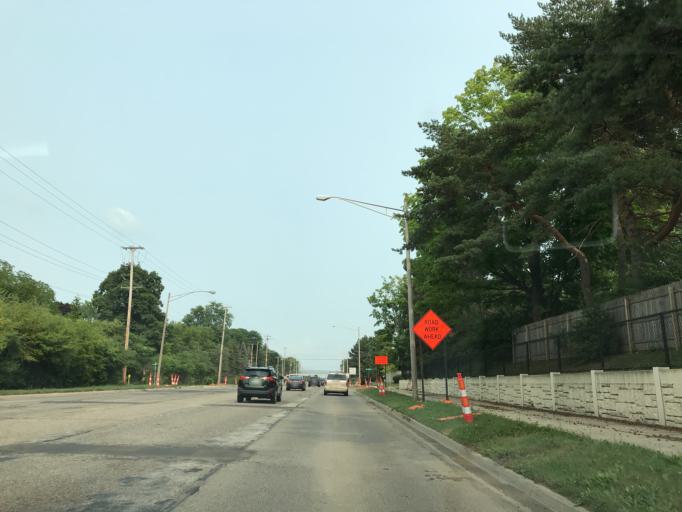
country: US
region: Michigan
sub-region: Ingham County
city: East Lansing
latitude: 42.7468
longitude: -84.4770
